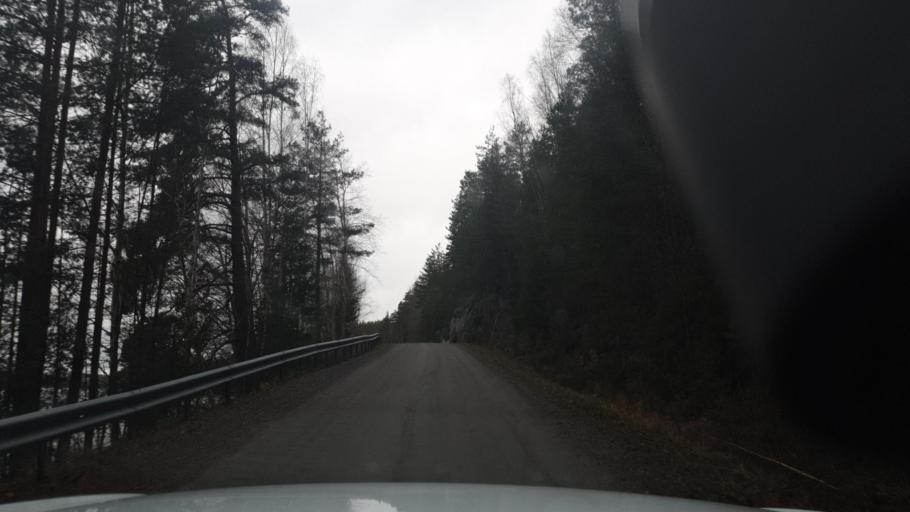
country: SE
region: Vaermland
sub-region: Sunne Kommun
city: Sunne
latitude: 59.6310
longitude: 13.0633
